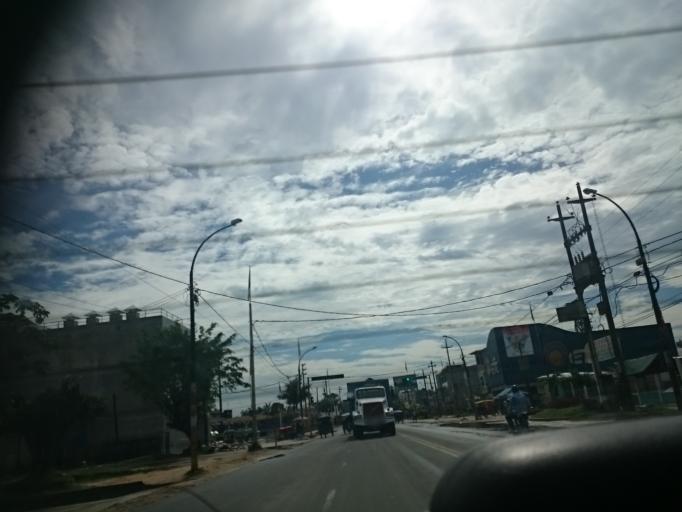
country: PE
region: Loreto
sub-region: Provincia de Maynas
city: Iquitos
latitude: -3.7762
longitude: -73.2898
